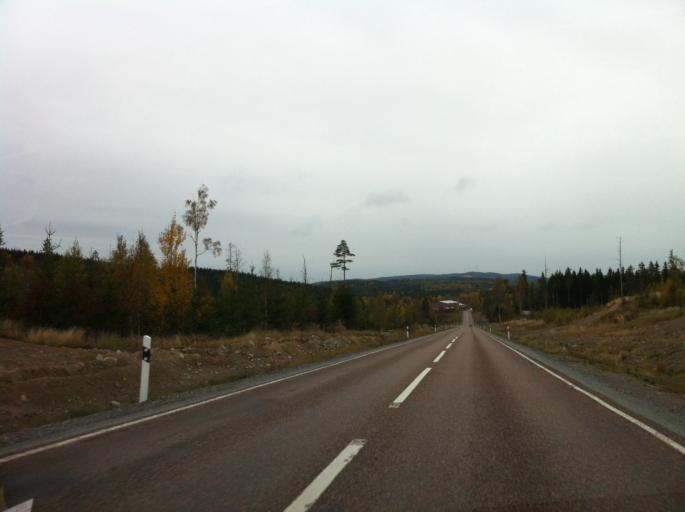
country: SE
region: Dalarna
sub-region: Ludvika Kommun
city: Grangesberg
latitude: 60.0207
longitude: 14.9823
